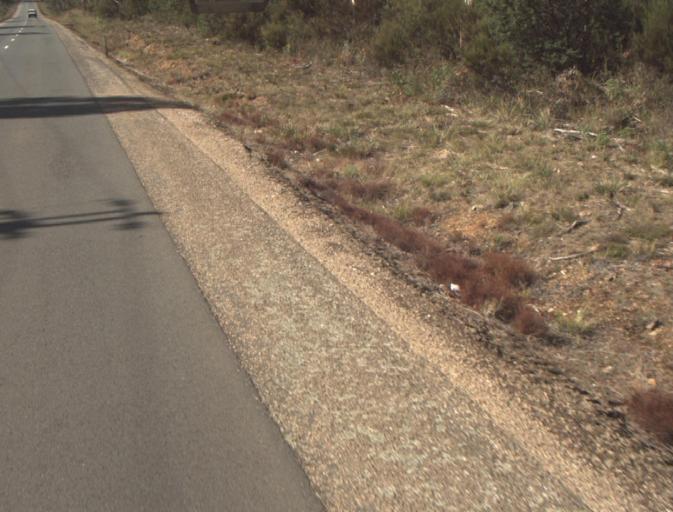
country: AU
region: Tasmania
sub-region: Launceston
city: Mayfield
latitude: -41.3181
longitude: 147.1913
